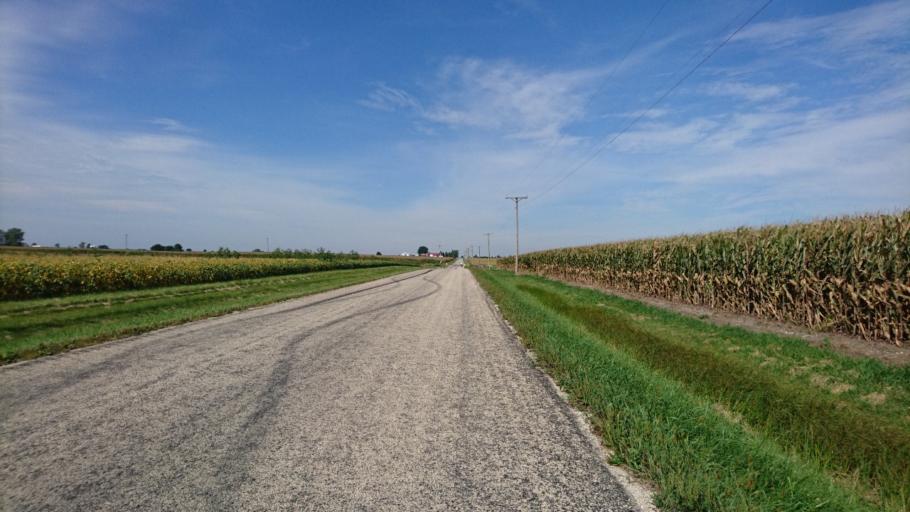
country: US
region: Illinois
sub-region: Will County
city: Elwood
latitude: 41.4160
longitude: -88.0557
